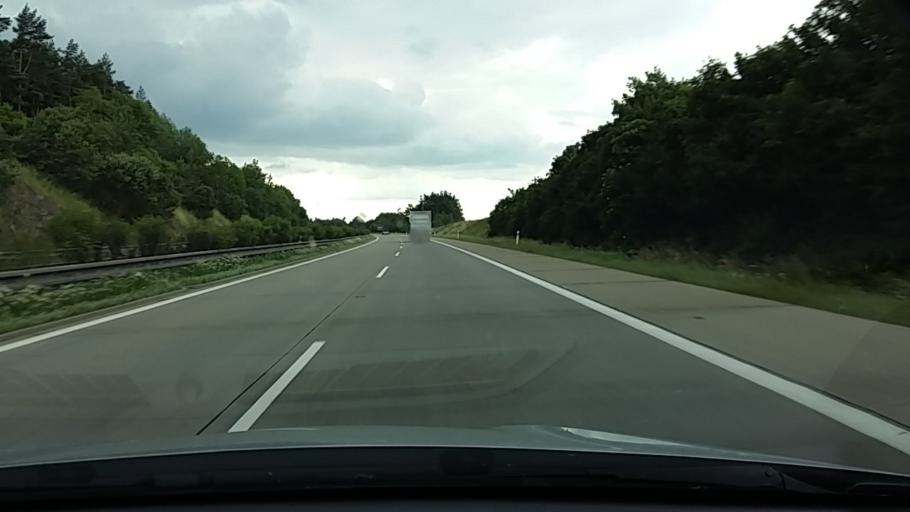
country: CZ
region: Plzensky
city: Bor
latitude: 49.7521
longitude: 12.8167
